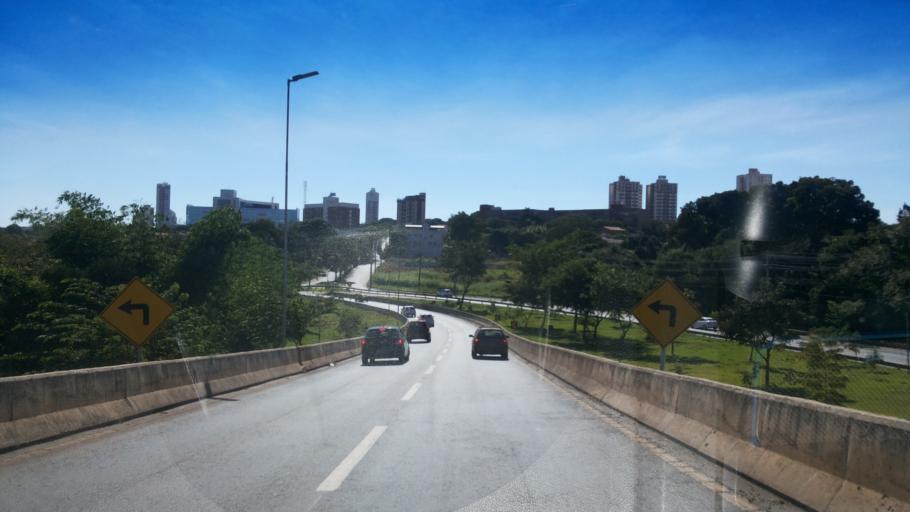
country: BR
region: Goias
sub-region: Goiania
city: Goiania
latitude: -16.6940
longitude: -49.2432
